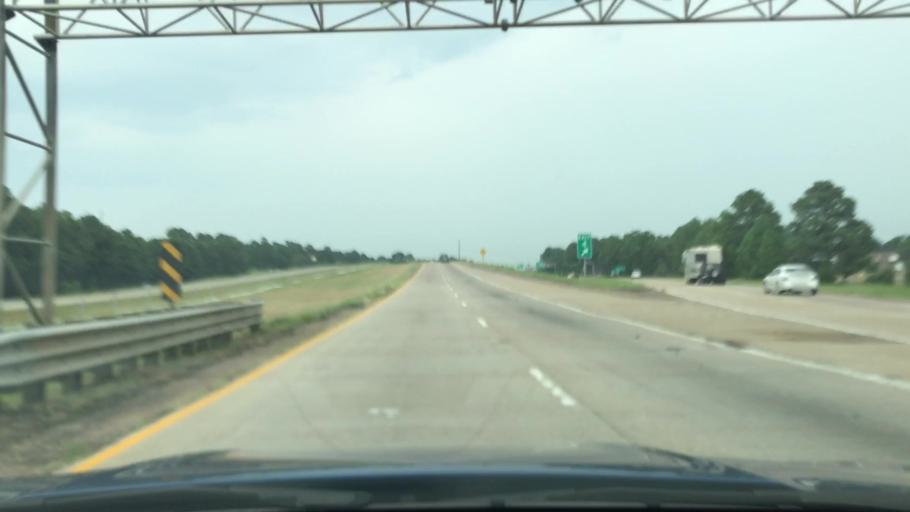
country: US
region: Louisiana
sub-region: Caddo Parish
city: Shreveport
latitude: 32.4171
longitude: -93.8017
